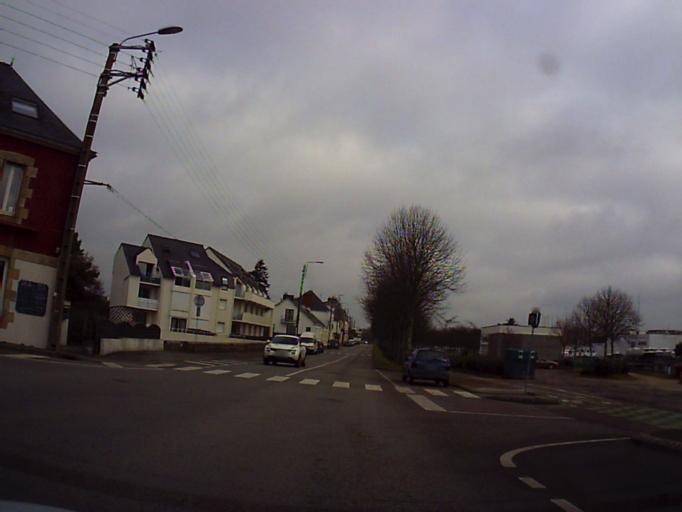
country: FR
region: Brittany
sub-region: Departement du Morbihan
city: Vannes
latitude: 47.6428
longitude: -2.7609
